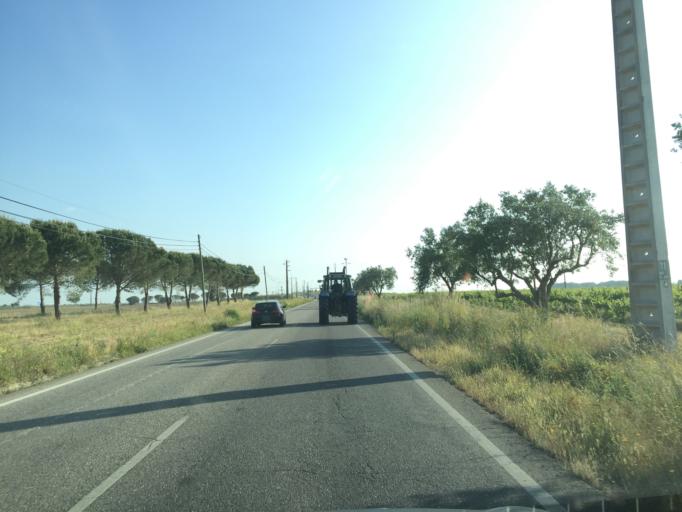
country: PT
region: Santarem
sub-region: Almeirim
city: Almeirim
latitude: 39.1952
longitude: -8.6441
